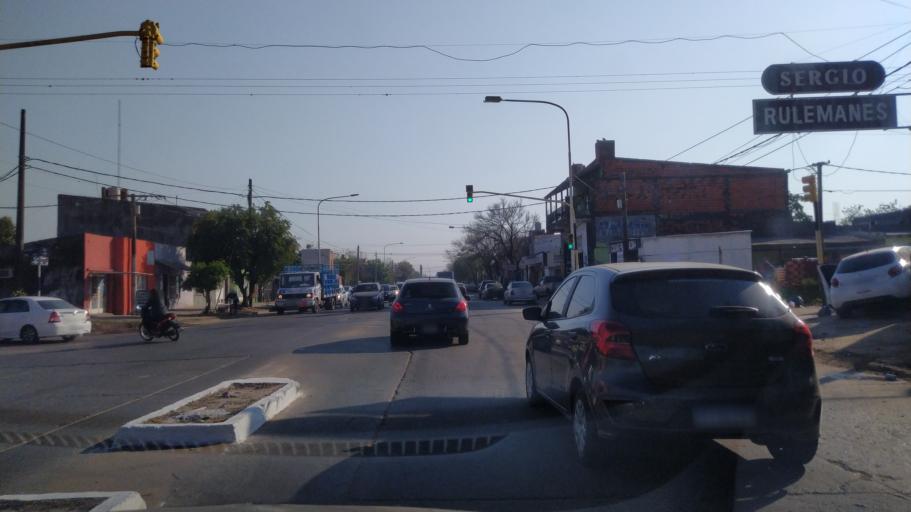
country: AR
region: Corrientes
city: Corrientes
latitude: -27.4832
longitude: -58.8156
